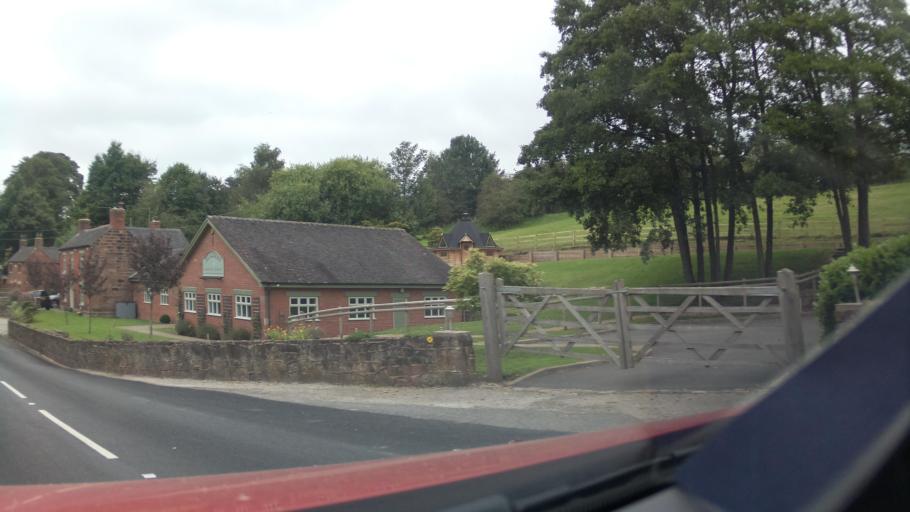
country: GB
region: England
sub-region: Staffordshire
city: Cheadle
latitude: 53.0222
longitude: -1.9444
